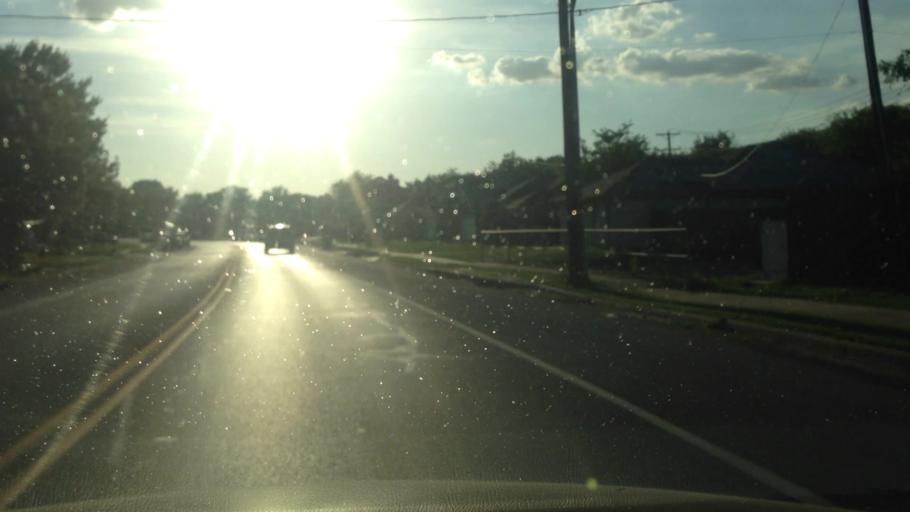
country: US
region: Texas
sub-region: Tarrant County
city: Watauga
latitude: 32.8746
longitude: -97.2425
